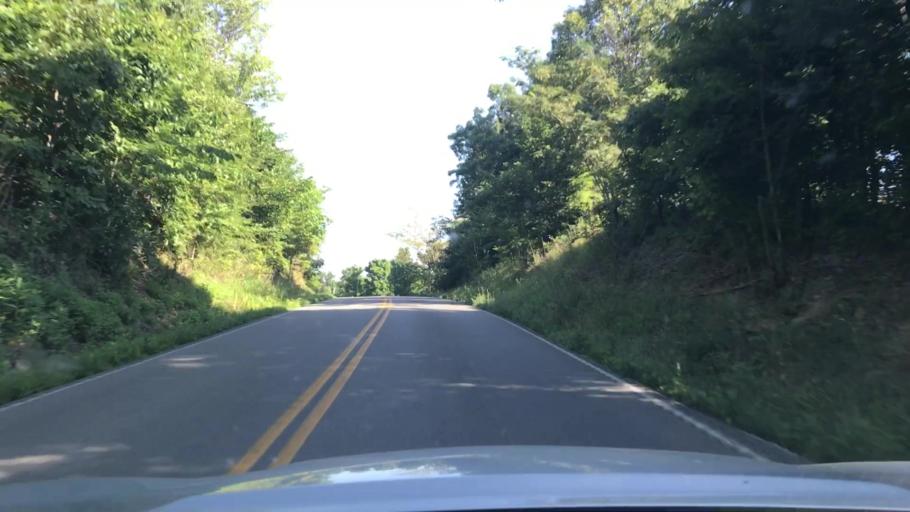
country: US
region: Kentucky
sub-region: Muhlenberg County
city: Greenville
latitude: 37.1132
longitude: -87.1279
